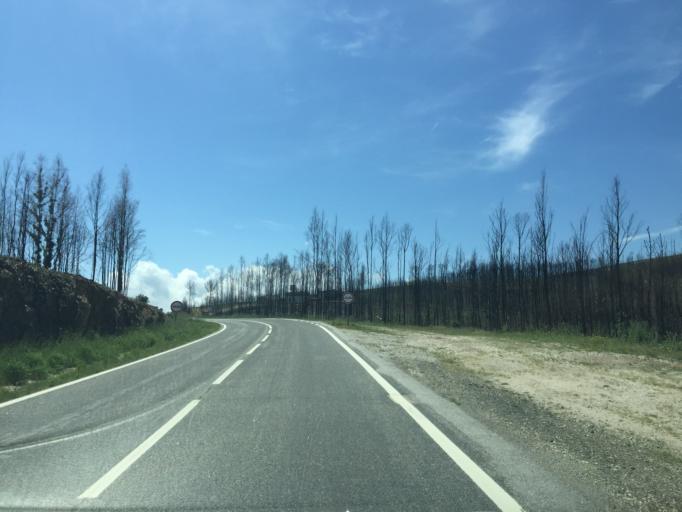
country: PT
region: Coimbra
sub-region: Pampilhosa da Serra
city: Pampilhosa da Serra
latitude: 40.0236
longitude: -7.9652
